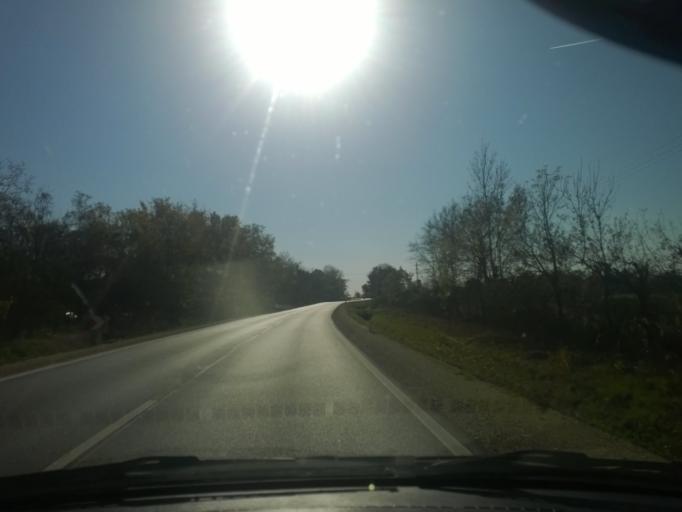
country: HU
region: Csongrad
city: Szentes
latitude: 46.6036
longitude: 20.2931
